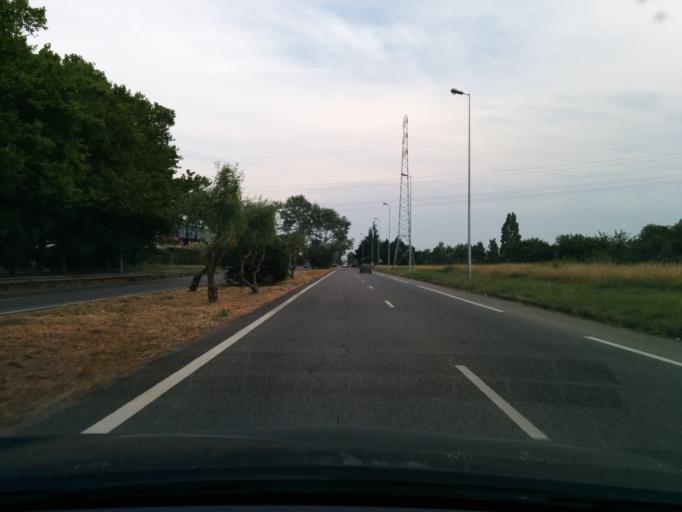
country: FR
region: Midi-Pyrenees
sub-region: Departement de la Haute-Garonne
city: Ramonville-Saint-Agne
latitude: 43.5465
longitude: 1.5018
